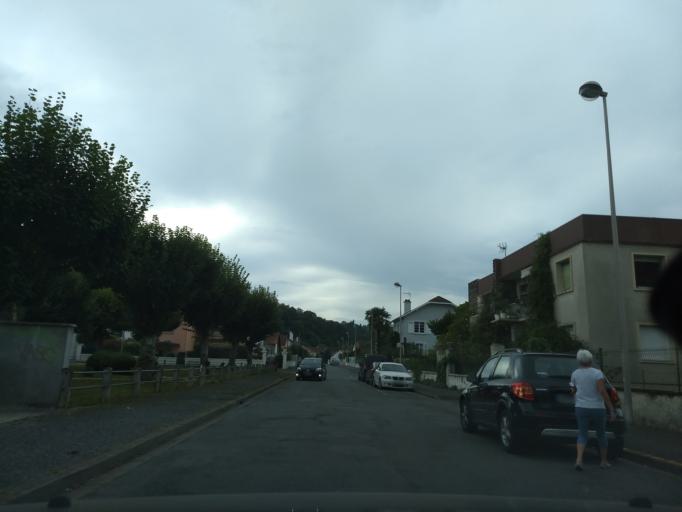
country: FR
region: Aquitaine
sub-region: Departement des Pyrenees-Atlantiques
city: Gelos
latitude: 43.2817
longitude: -0.3767
